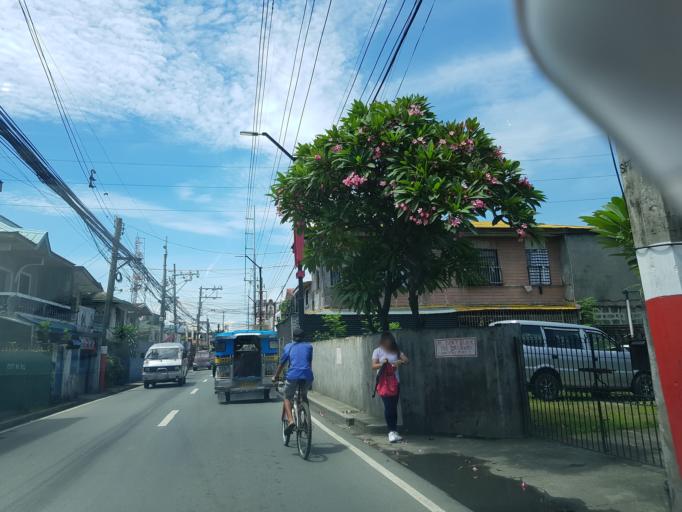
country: PH
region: Calabarzon
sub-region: Province of Rizal
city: Taguig
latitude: 14.5134
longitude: 121.0702
